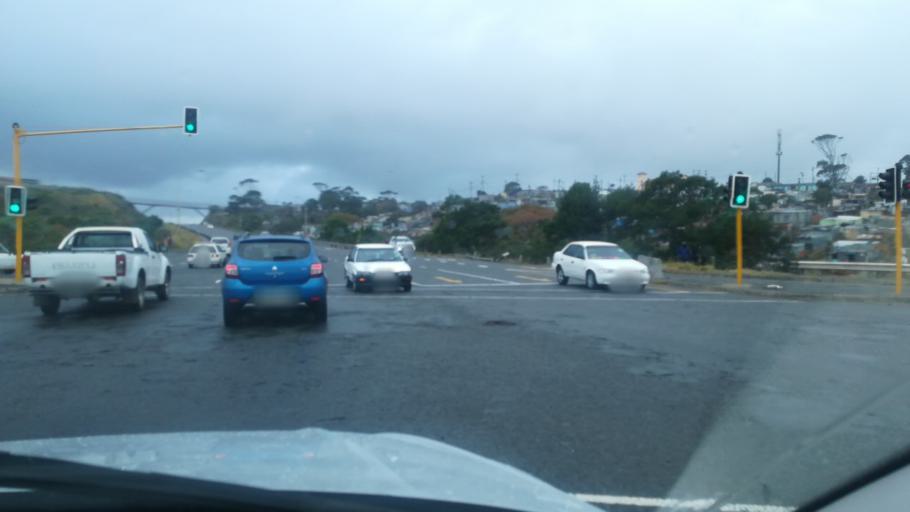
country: ZA
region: Eastern Cape
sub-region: Buffalo City Metropolitan Municipality
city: East London
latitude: -33.0052
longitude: 27.8712
